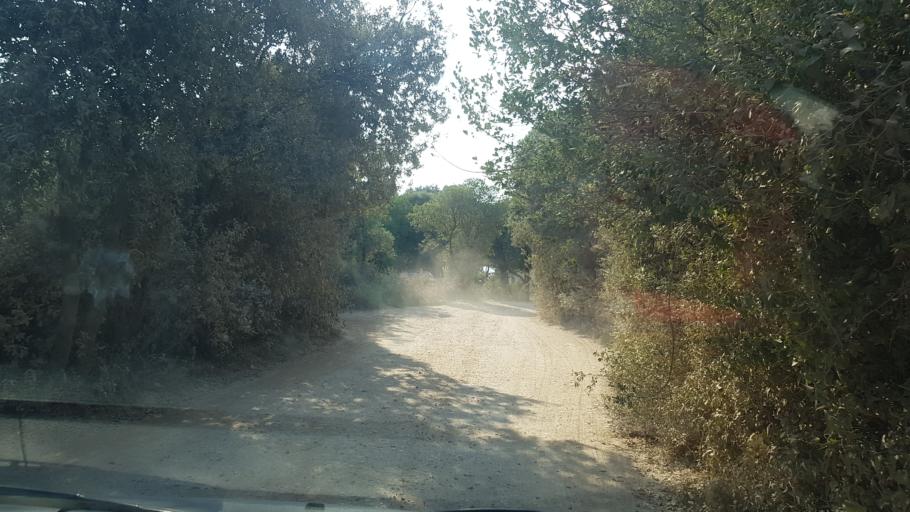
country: HR
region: Istarska
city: Vrsar
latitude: 45.1108
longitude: 13.6138
